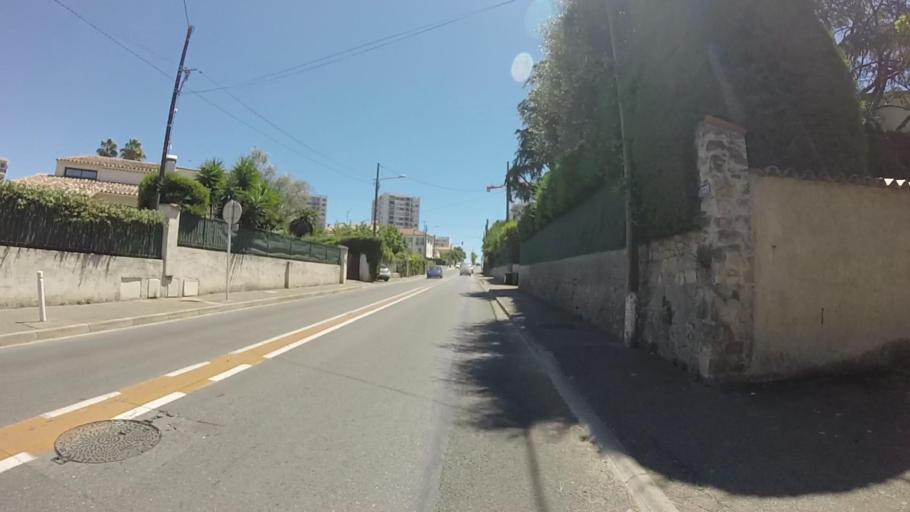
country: FR
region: Provence-Alpes-Cote d'Azur
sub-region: Departement des Alpes-Maritimes
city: Antibes
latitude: 43.5840
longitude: 7.1055
